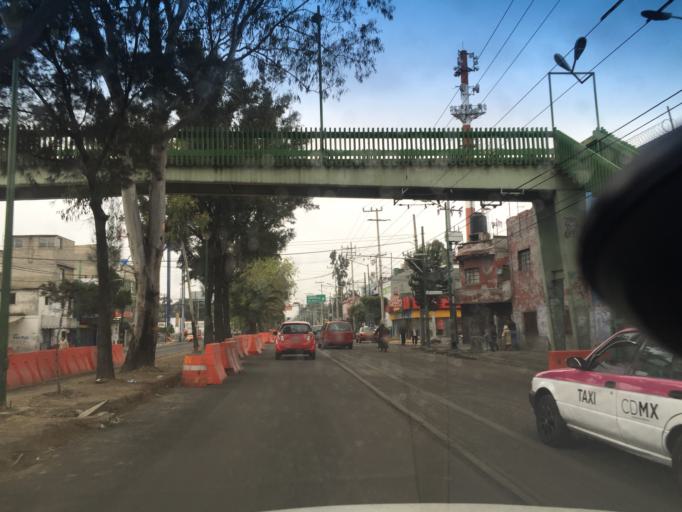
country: MX
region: Mexico City
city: Gustavo A. Madero
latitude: 19.4757
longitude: -99.0895
